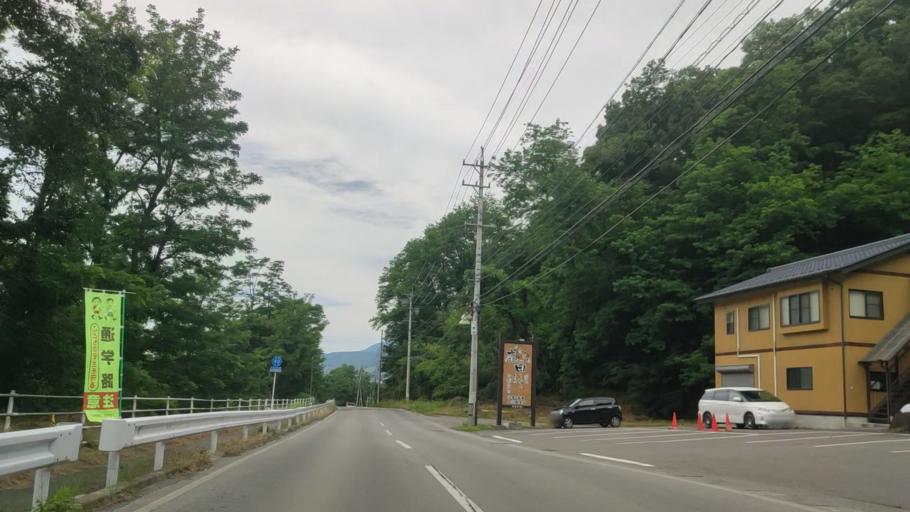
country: JP
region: Nagano
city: Kamimaruko
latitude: 36.3342
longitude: 138.3515
